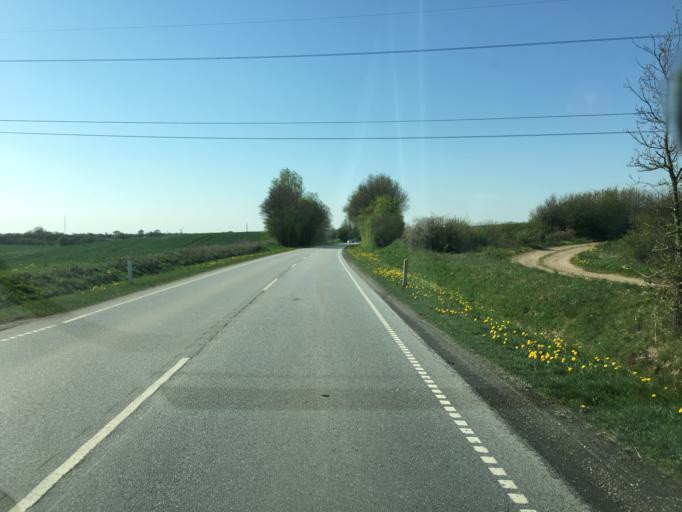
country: DK
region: South Denmark
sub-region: Haderslev Kommune
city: Vojens
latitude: 55.2952
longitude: 9.3854
